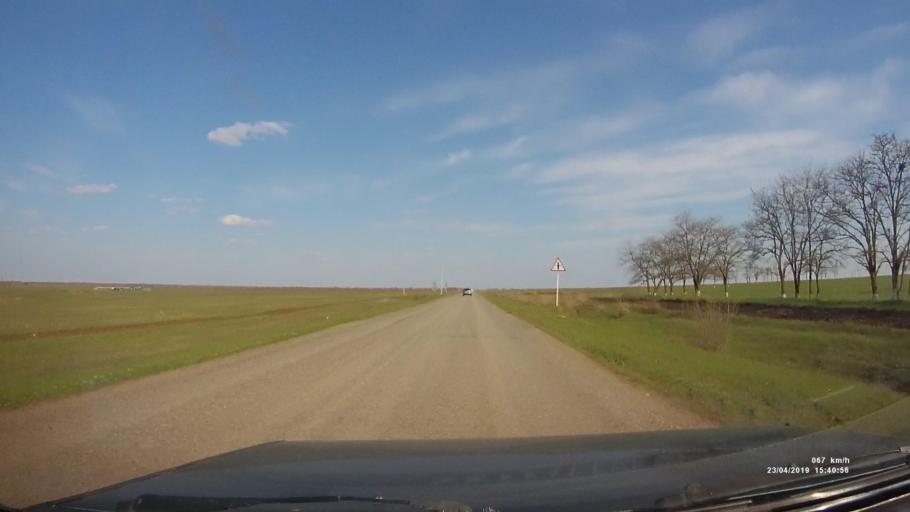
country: RU
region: Rostov
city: Remontnoye
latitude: 46.5532
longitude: 43.0441
